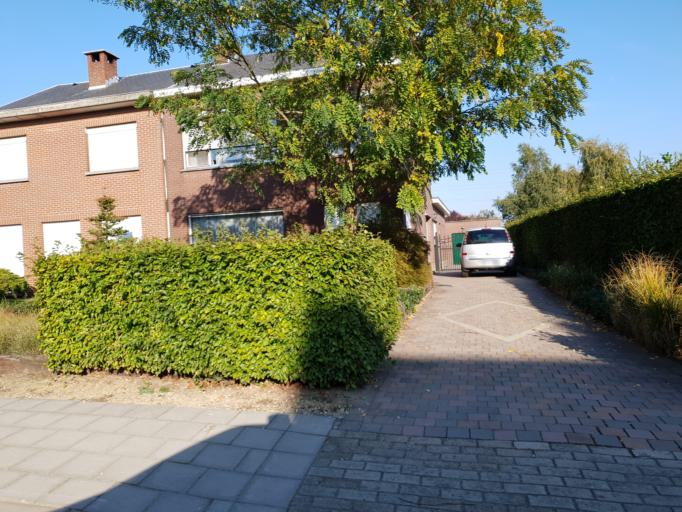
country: BE
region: Flanders
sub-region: Provincie Antwerpen
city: Boechout
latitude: 51.1564
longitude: 4.5144
